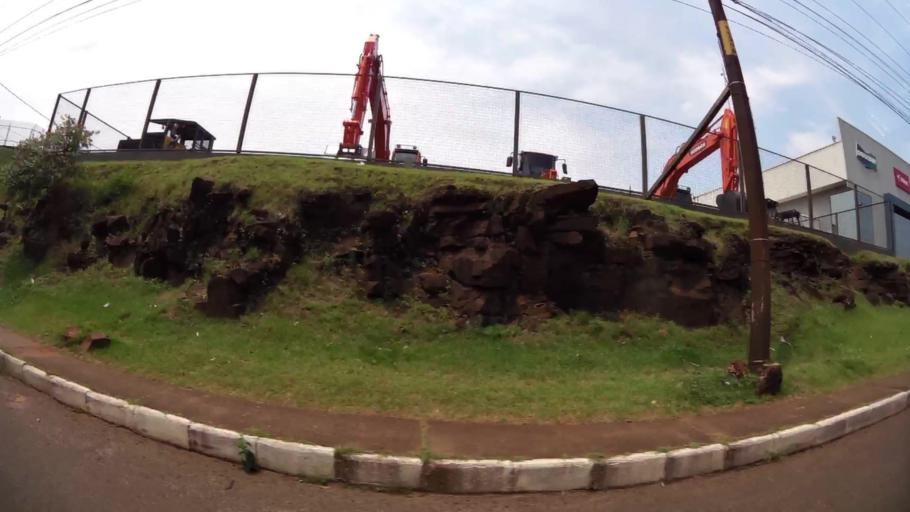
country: PY
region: Alto Parana
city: Ciudad del Este
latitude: -25.4950
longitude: -54.6335
